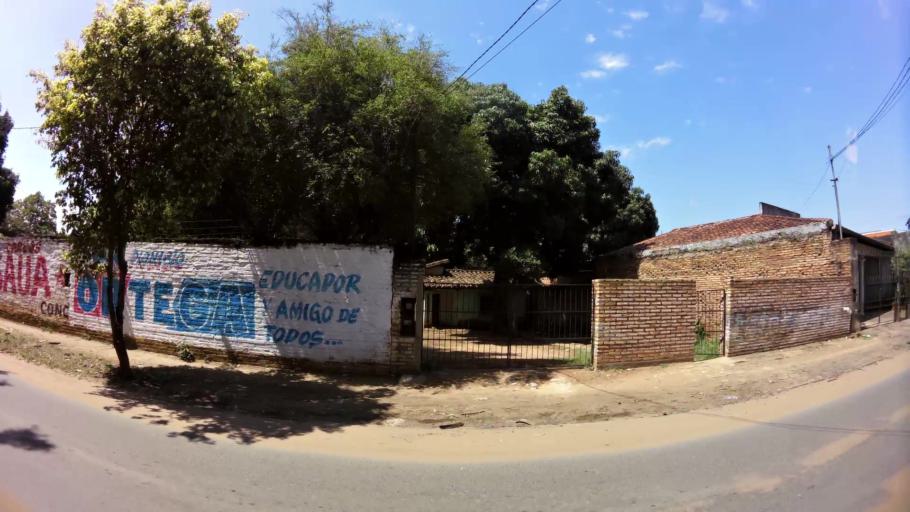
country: PY
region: Central
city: Fernando de la Mora
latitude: -25.3258
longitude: -57.5545
